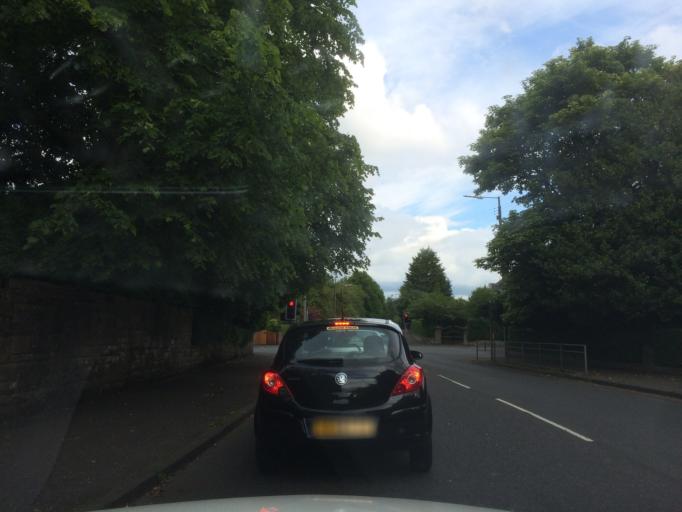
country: GB
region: Scotland
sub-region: East Renfrewshire
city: Giffnock
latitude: 55.8137
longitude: -4.2780
